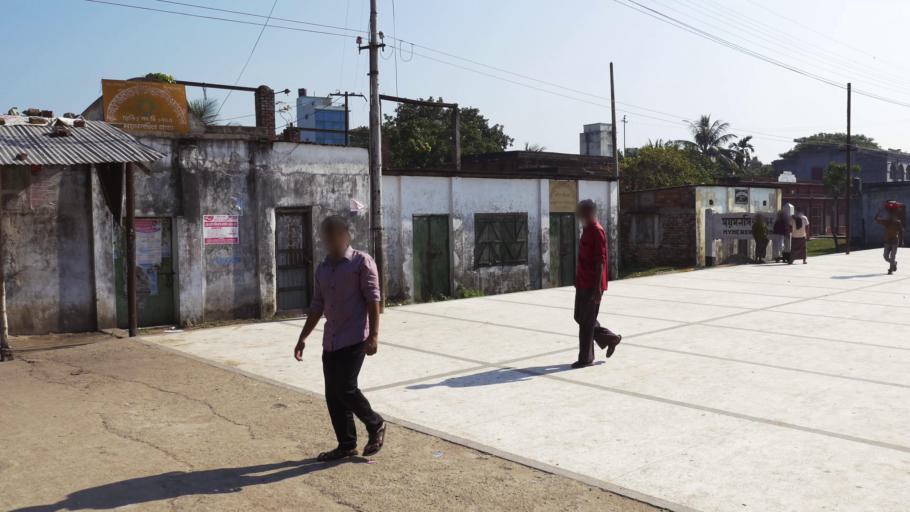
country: BD
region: Dhaka
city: Mymensingh
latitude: 24.6964
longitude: 90.4517
